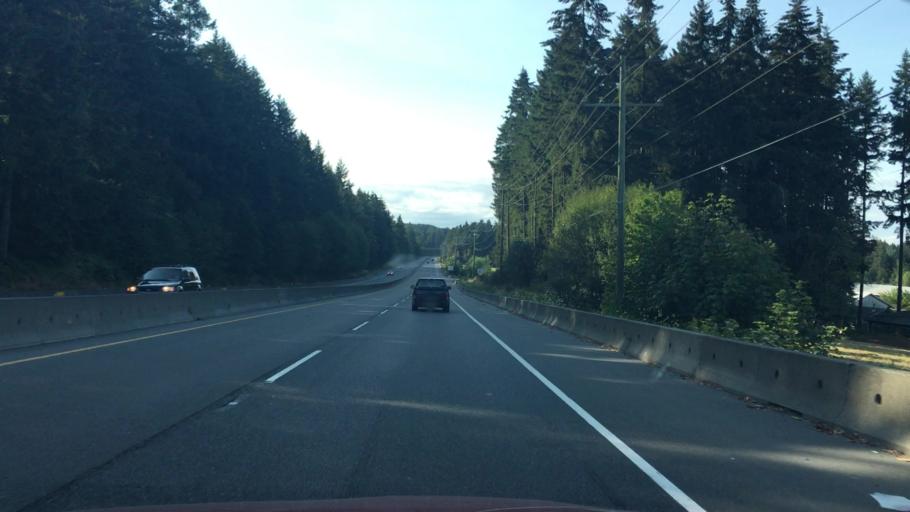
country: CA
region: British Columbia
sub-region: Cowichan Valley Regional District
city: Ladysmith
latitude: 48.9402
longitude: -123.7662
